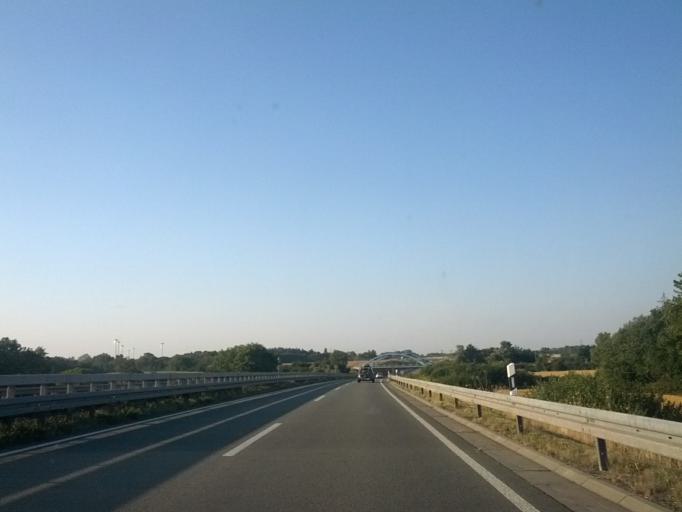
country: DE
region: Mecklenburg-Vorpommern
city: Brandshagen
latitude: 54.2256
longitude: 13.1545
